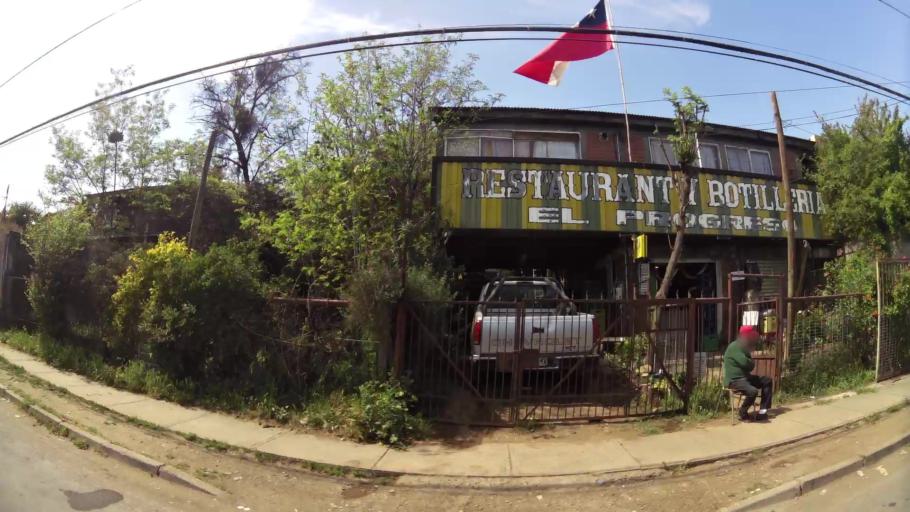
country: CL
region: Santiago Metropolitan
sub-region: Provincia de Santiago
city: Villa Presidente Frei, Nunoa, Santiago, Chile
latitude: -33.4723
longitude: -70.5269
